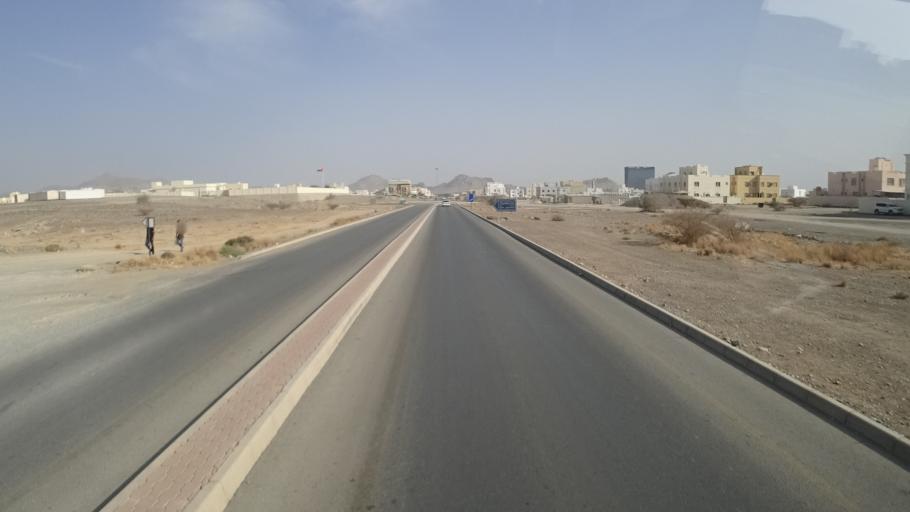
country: OM
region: Muhafazat ad Dakhiliyah
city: Nizwa
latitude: 22.8746
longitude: 57.5410
